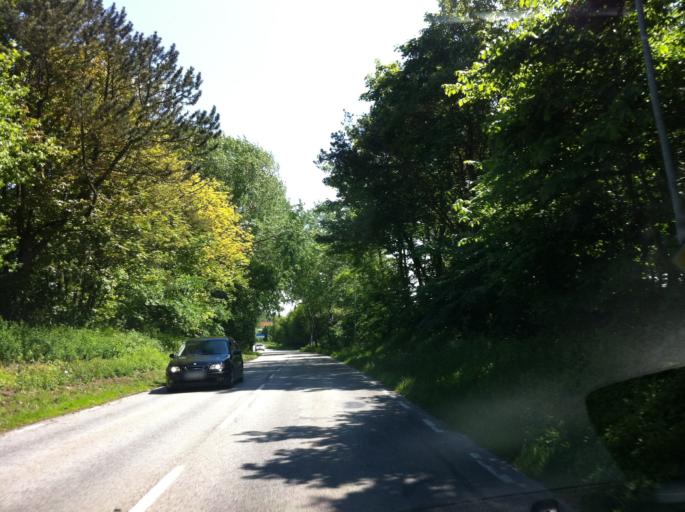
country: SE
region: Skane
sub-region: Kavlinge Kommun
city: Hofterup
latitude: 55.7978
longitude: 12.9905
